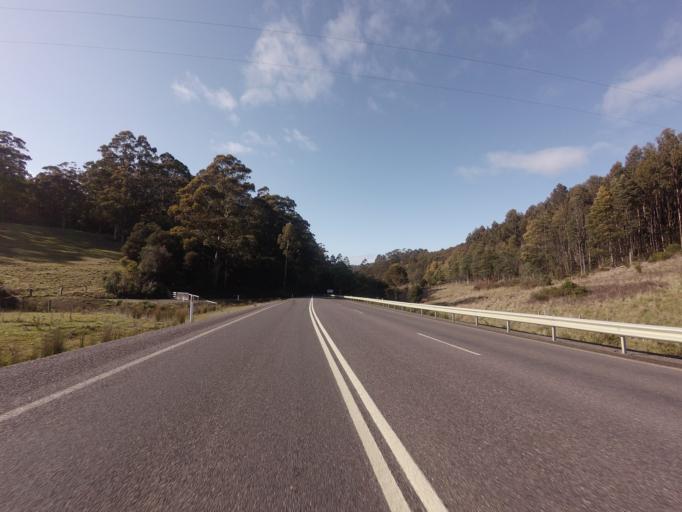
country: AU
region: Tasmania
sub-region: Huon Valley
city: Geeveston
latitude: -43.2585
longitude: 147.0055
